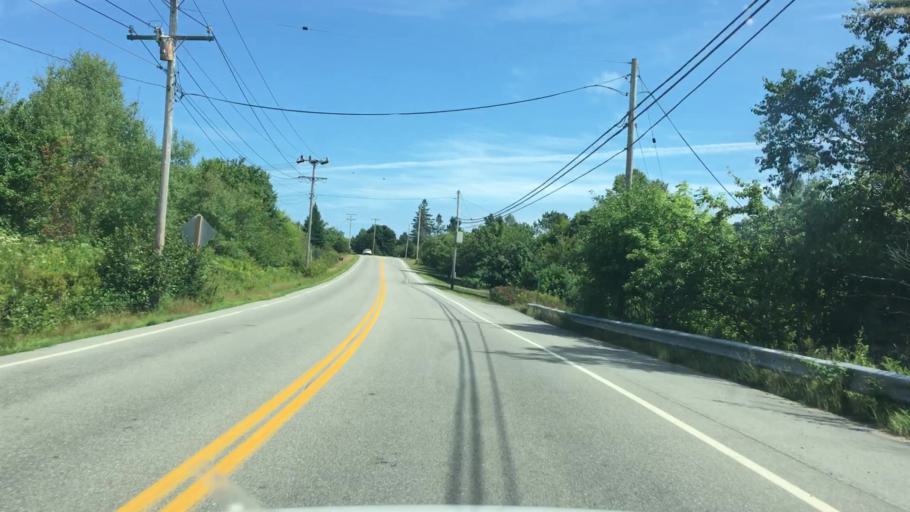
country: US
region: Maine
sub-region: Washington County
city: Eastport
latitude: 44.9138
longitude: -67.0059
